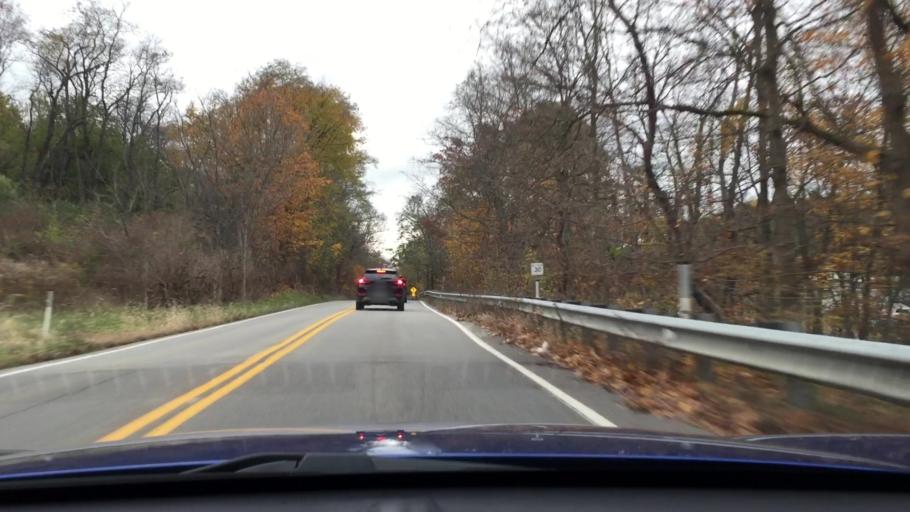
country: US
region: Pennsylvania
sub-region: Washington County
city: McGovern
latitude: 40.2085
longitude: -80.2246
